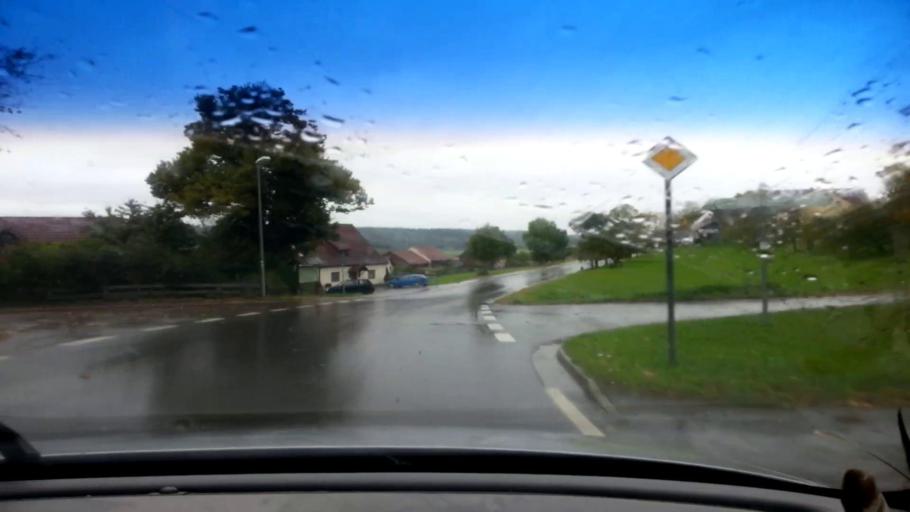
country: DE
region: Bavaria
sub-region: Upper Franconia
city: Konigsfeld
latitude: 49.9318
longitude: 11.1519
